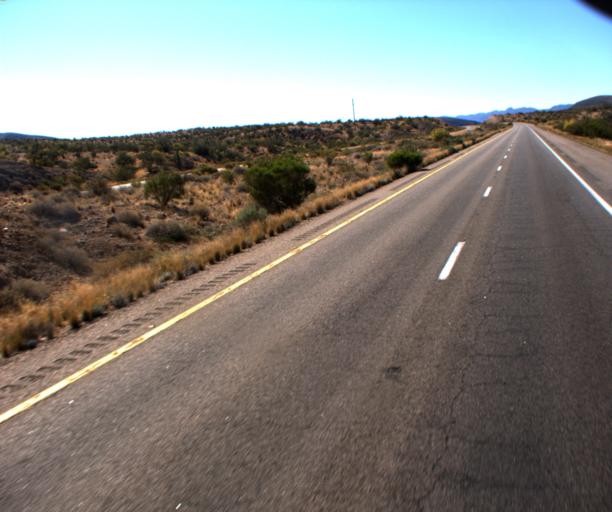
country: US
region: Arizona
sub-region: Yavapai County
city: Bagdad
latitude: 34.6005
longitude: -113.5193
